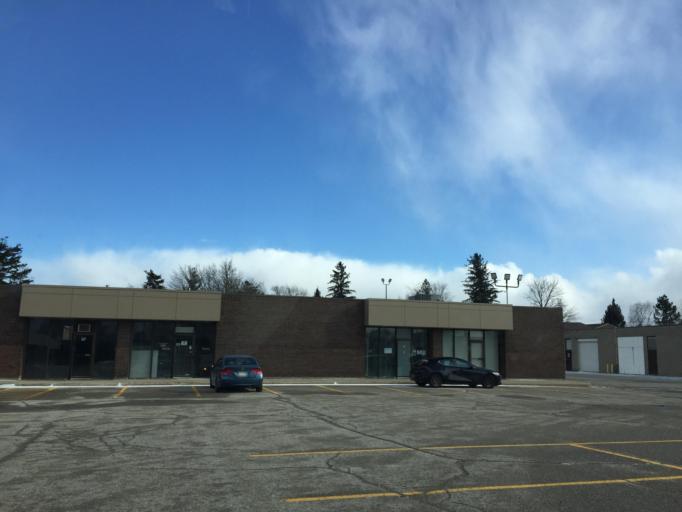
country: CA
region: Ontario
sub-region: Wellington County
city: Guelph
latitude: 43.5448
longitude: -80.2852
